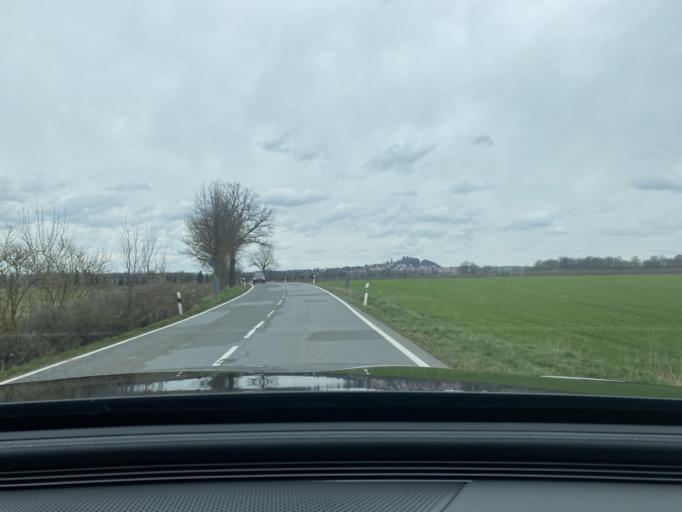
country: DE
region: Saxony
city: Stolpen
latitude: 51.0350
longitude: 14.0473
